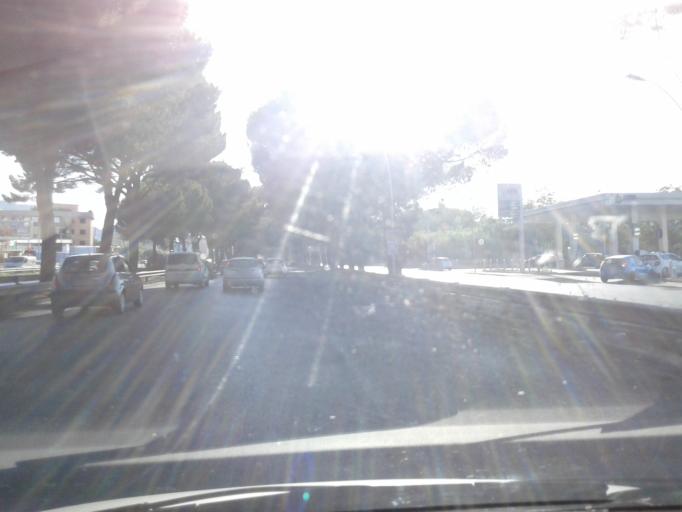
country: IT
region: Sicily
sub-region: Palermo
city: Ciaculli
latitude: 38.0898
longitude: 13.3727
